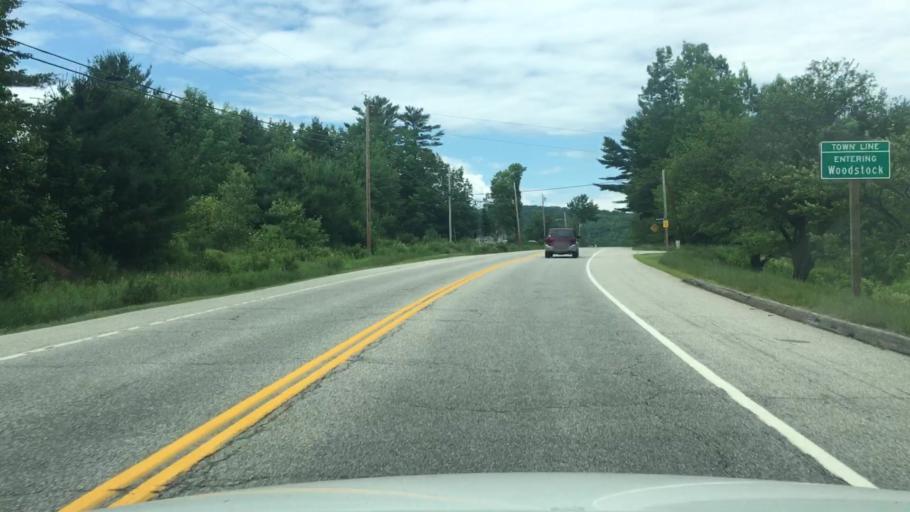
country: US
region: Maine
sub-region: Oxford County
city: West Paris
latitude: 44.3443
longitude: -70.5624
